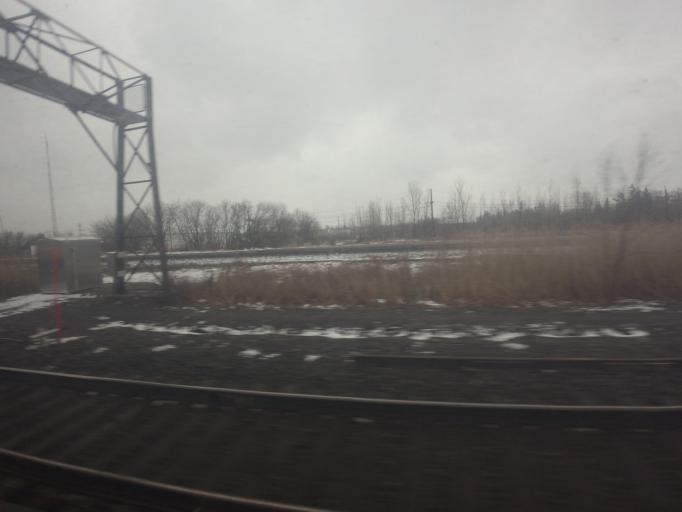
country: CA
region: Ontario
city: Quinte West
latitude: 44.0382
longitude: -77.7338
